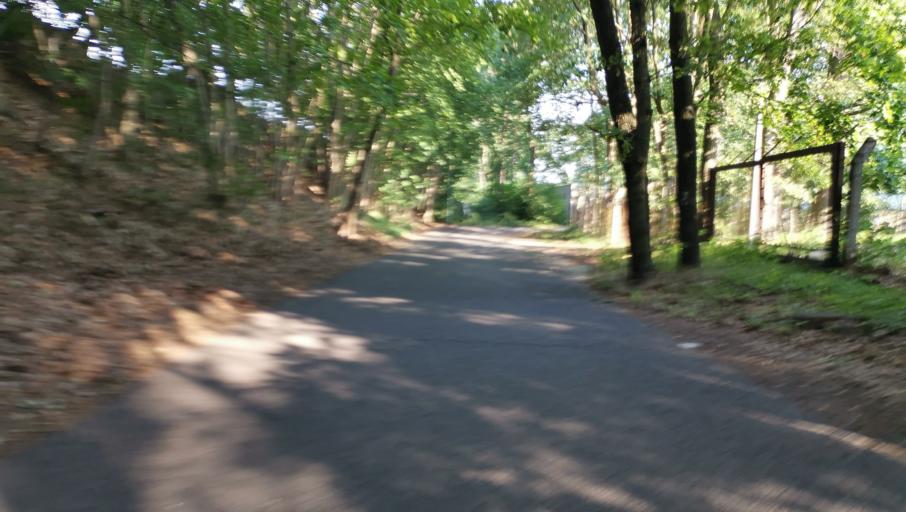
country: DE
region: Brandenburg
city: Potsdam
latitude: 52.3719
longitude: 13.0133
